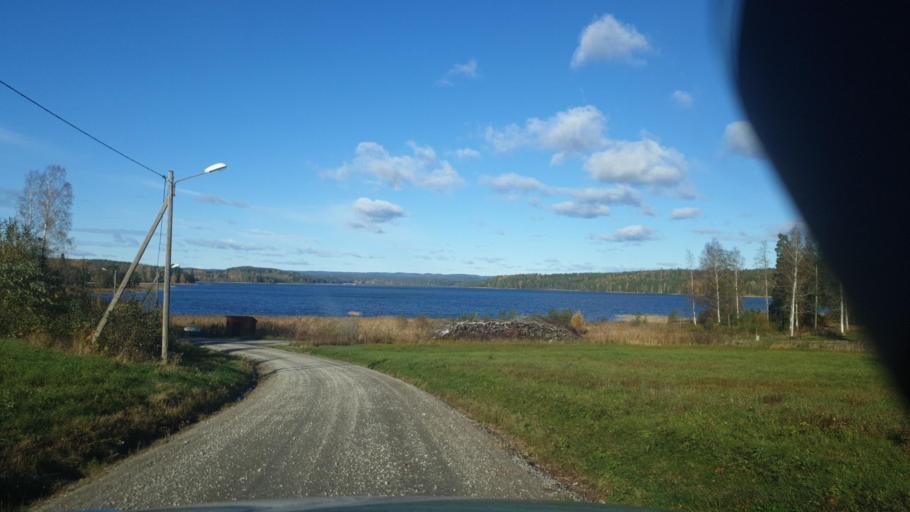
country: SE
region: Vaermland
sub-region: Karlstads Kommun
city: Edsvalla
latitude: 59.6034
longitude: 12.9199
